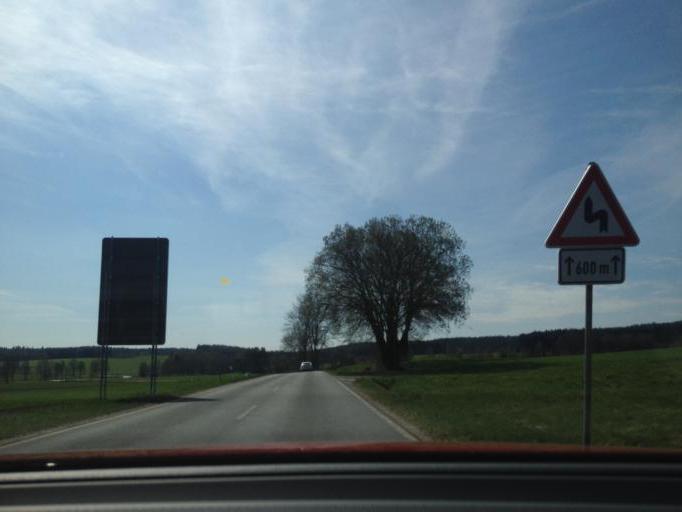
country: DE
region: Bavaria
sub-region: Upper Franconia
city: Weissenstadt
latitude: 50.0957
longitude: 11.8922
